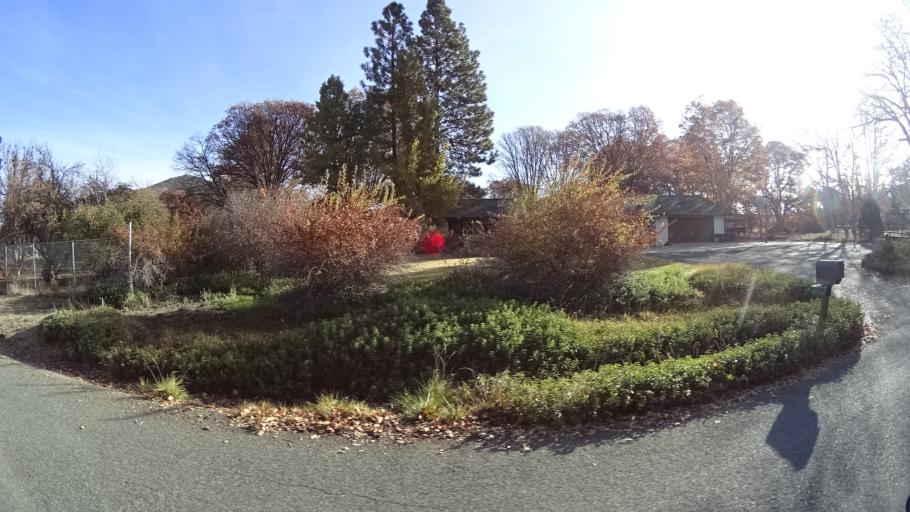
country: US
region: California
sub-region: Siskiyou County
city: Yreka
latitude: 41.6763
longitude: -122.6356
